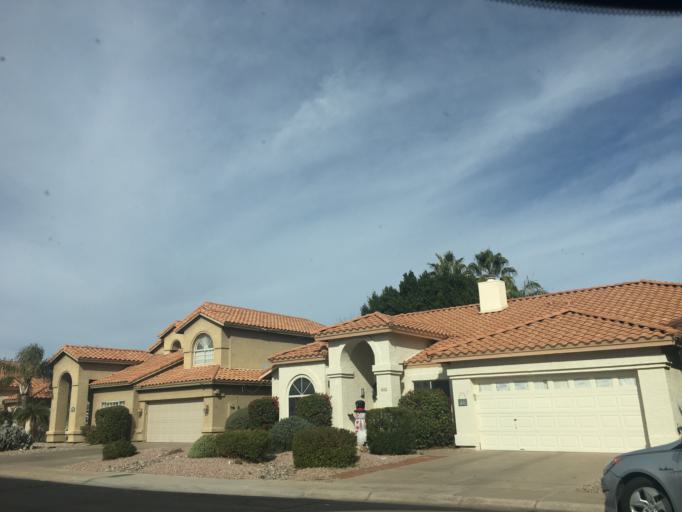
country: US
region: Arizona
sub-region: Maricopa County
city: Gilbert
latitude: 33.3472
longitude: -111.8037
